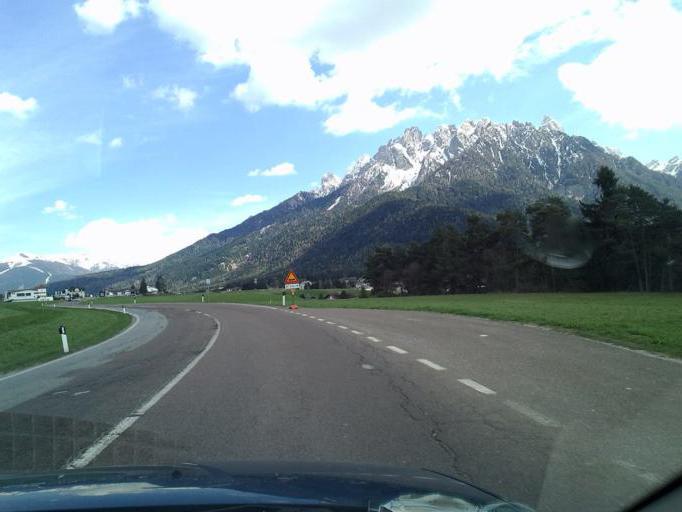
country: IT
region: Trentino-Alto Adige
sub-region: Bolzano
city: Dobbiaco
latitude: 46.7304
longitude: 12.2099
